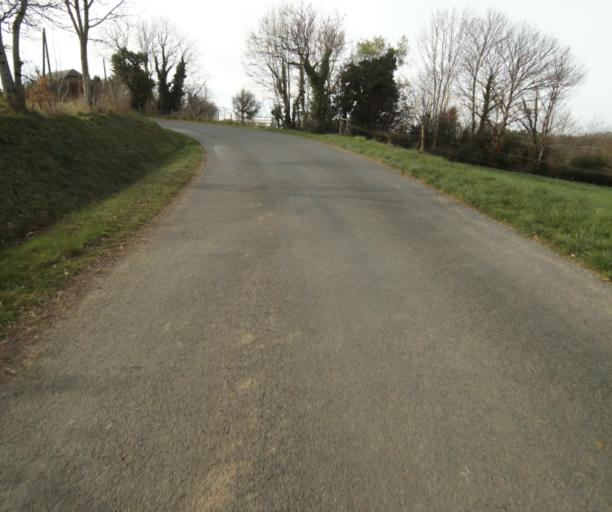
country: FR
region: Limousin
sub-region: Departement de la Correze
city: Chamboulive
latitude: 45.4149
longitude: 1.7836
